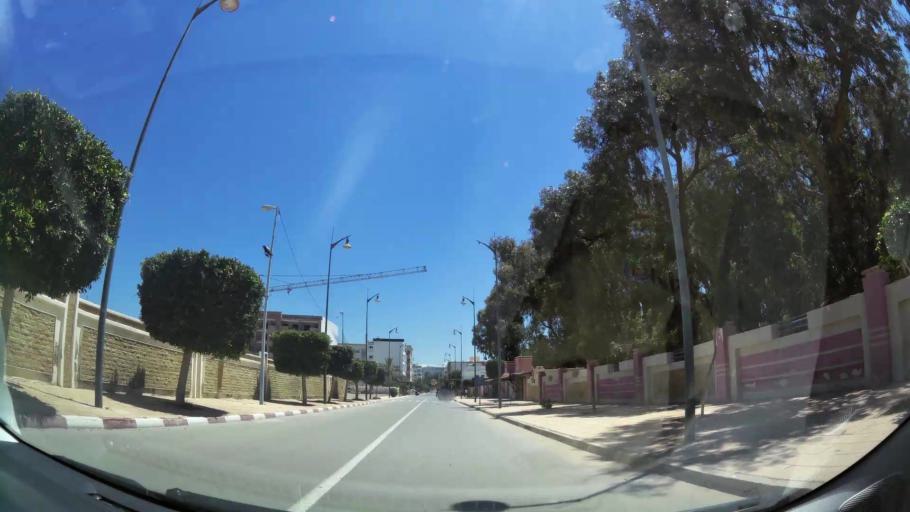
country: MA
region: Oriental
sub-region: Berkane-Taourirt
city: Madagh
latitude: 35.0852
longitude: -2.2263
